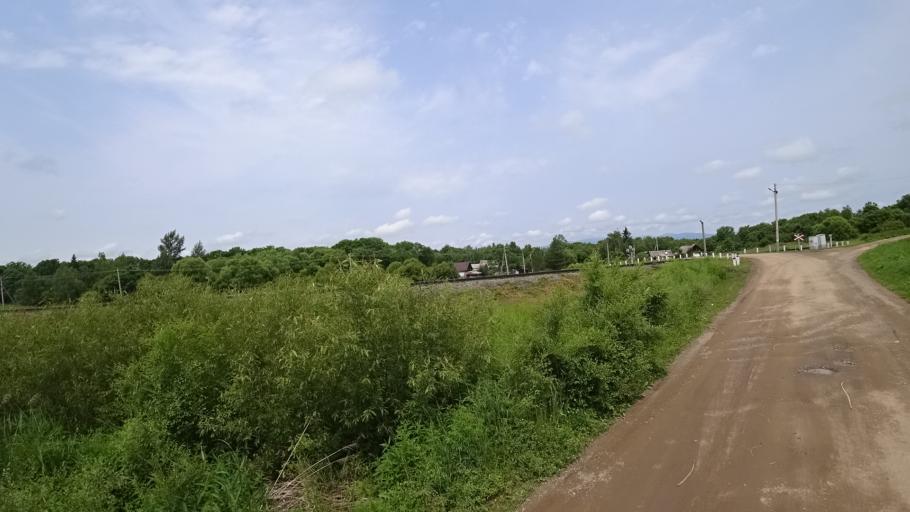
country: RU
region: Primorskiy
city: Novosysoyevka
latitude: 44.2526
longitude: 133.3753
